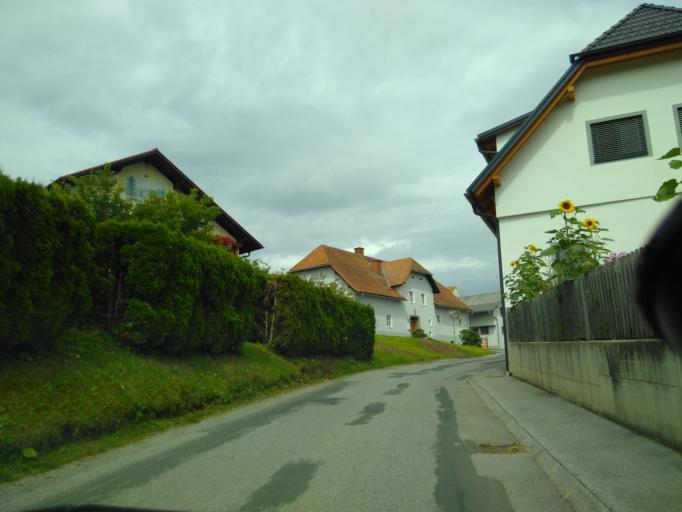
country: AT
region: Styria
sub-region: Politischer Bezirk Graz-Umgebung
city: Semriach
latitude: 47.2351
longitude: 15.3950
